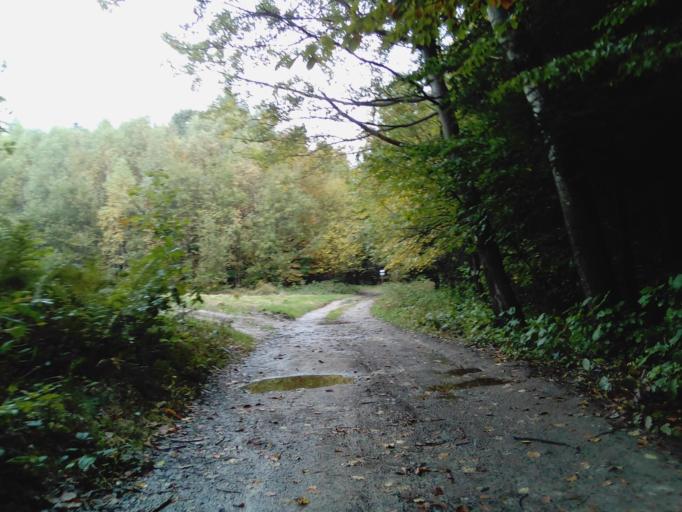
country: PL
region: Subcarpathian Voivodeship
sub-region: Powiat strzyzowski
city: Gwoznica Gorna
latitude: 49.8386
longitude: 22.0216
